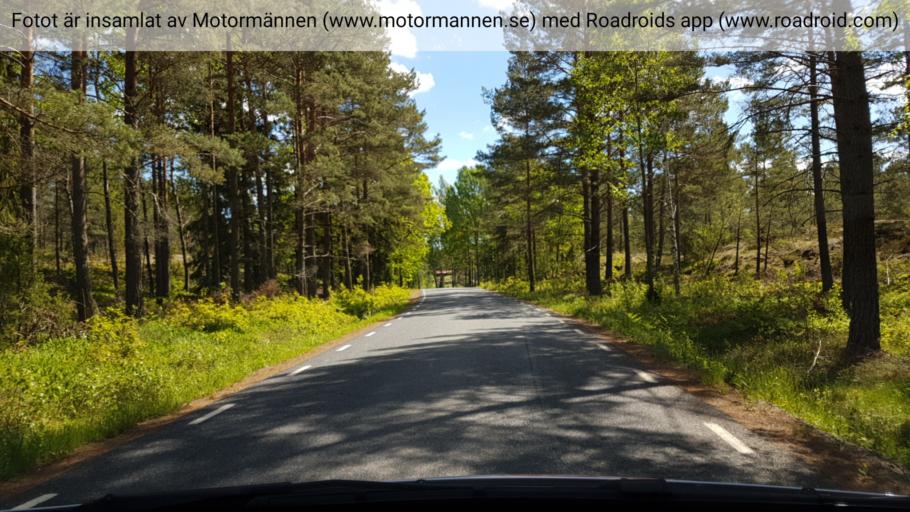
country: SE
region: Kalmar
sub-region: Vasterviks Kommun
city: Vaestervik
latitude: 57.9439
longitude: 16.6623
